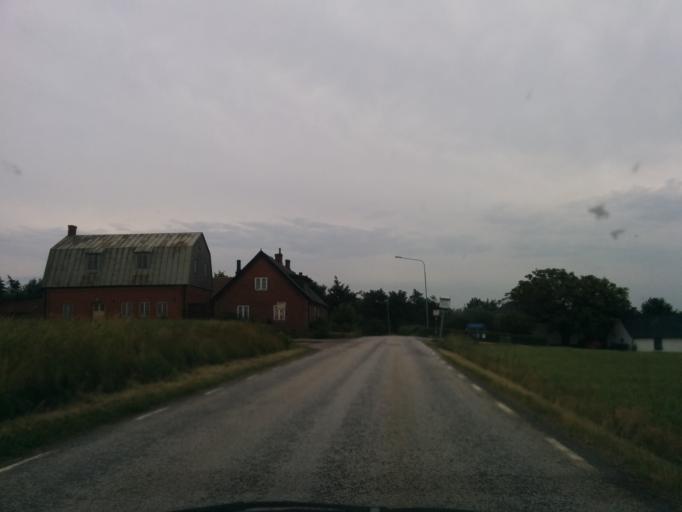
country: SE
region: Skane
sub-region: Lunds Kommun
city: Genarp
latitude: 55.6426
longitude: 13.3520
